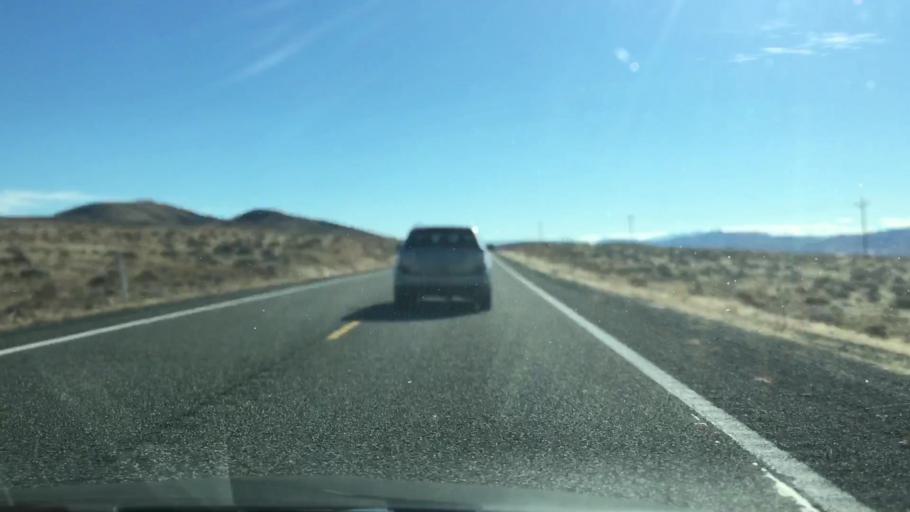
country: US
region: Nevada
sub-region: Lyon County
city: Silver Springs
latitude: 39.2007
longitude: -119.2135
